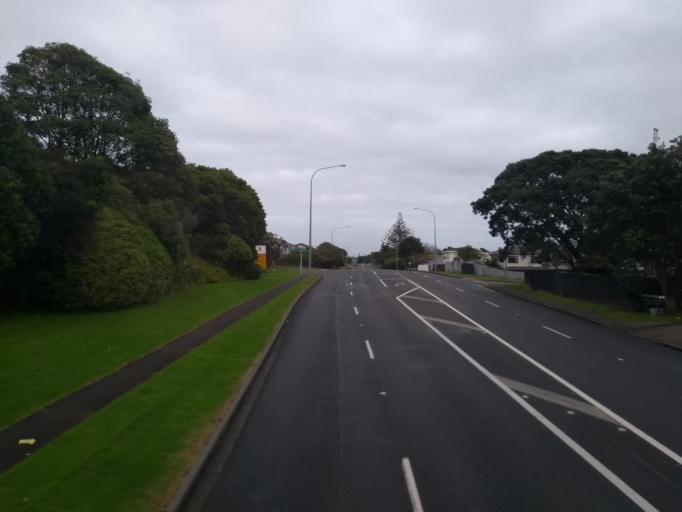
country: NZ
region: Auckland
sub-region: Auckland
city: Tamaki
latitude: -36.8973
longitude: 174.8270
